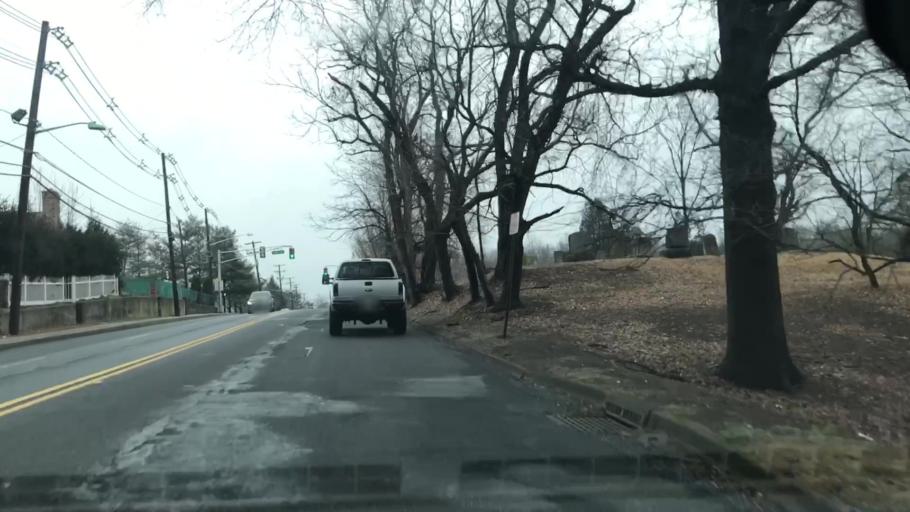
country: US
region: New Jersey
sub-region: Bergen County
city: Emerson
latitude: 40.9850
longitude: -74.0210
